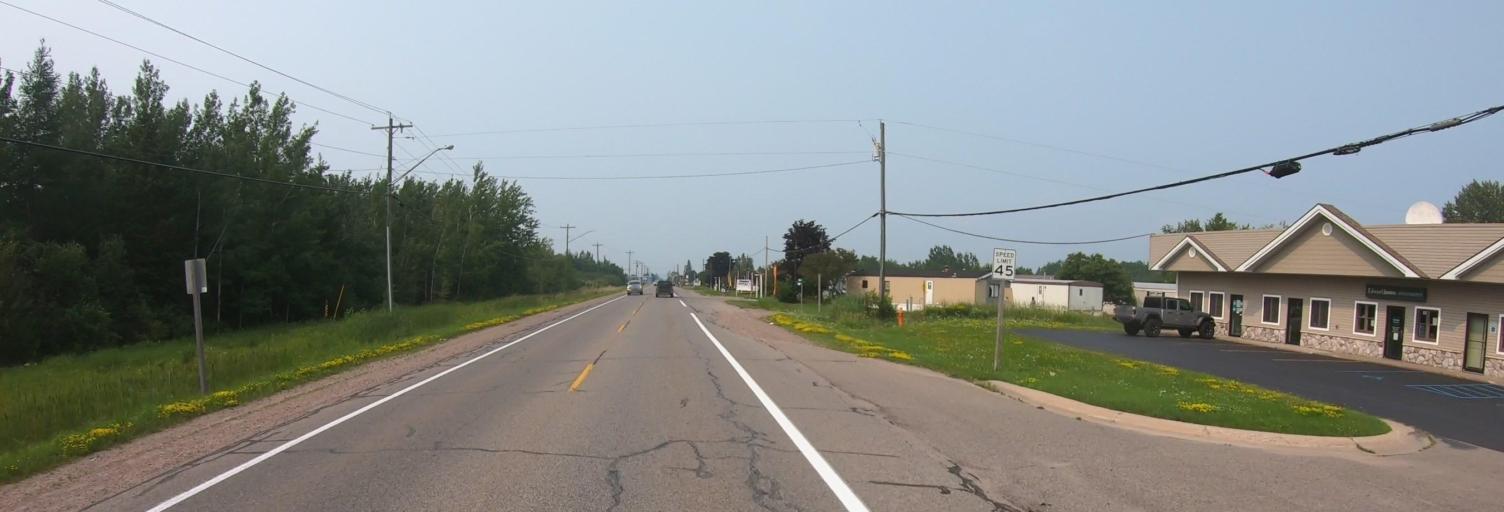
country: US
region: Michigan
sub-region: Chippewa County
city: Sault Ste. Marie
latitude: 46.4679
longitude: -84.3540
